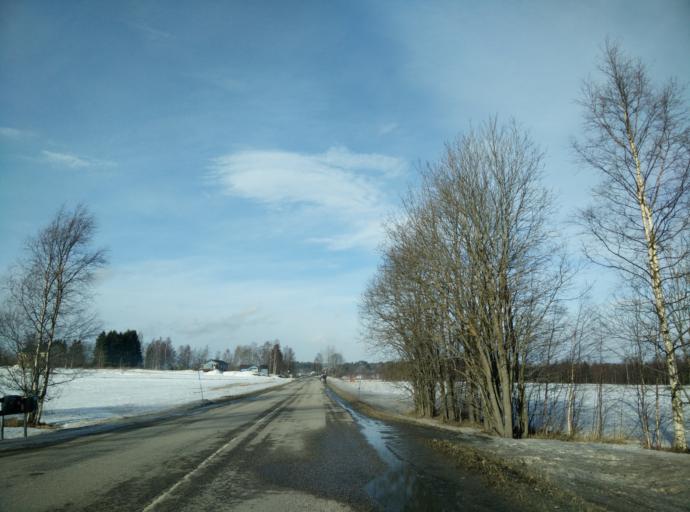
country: SE
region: Vaesternorrland
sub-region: Sundsvalls Kommun
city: Njurundabommen
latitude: 62.2418
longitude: 17.3800
